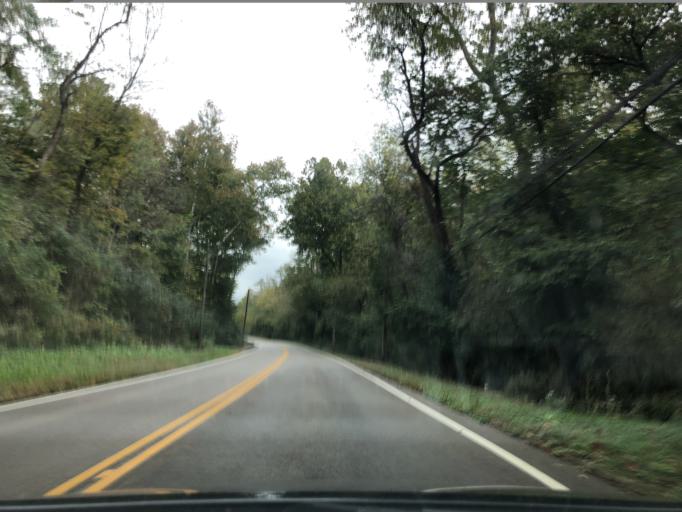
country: US
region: Ohio
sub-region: Hamilton County
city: Mariemont
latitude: 39.1653
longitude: -84.3784
